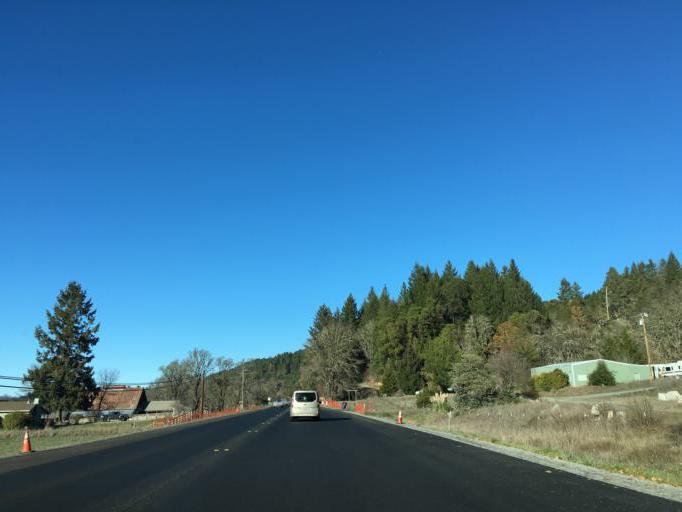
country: US
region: California
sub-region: Mendocino County
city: Laytonville
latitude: 39.6744
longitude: -123.4756
